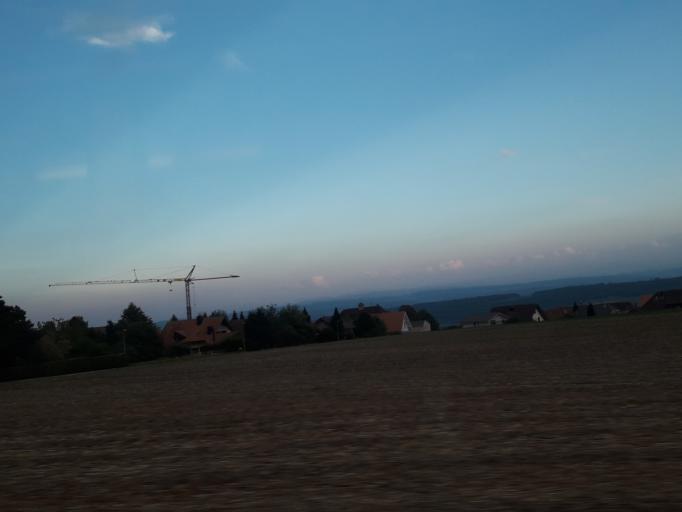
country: CH
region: Solothurn
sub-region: Bezirk Lebern
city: Selzach
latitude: 47.2277
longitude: 7.4697
